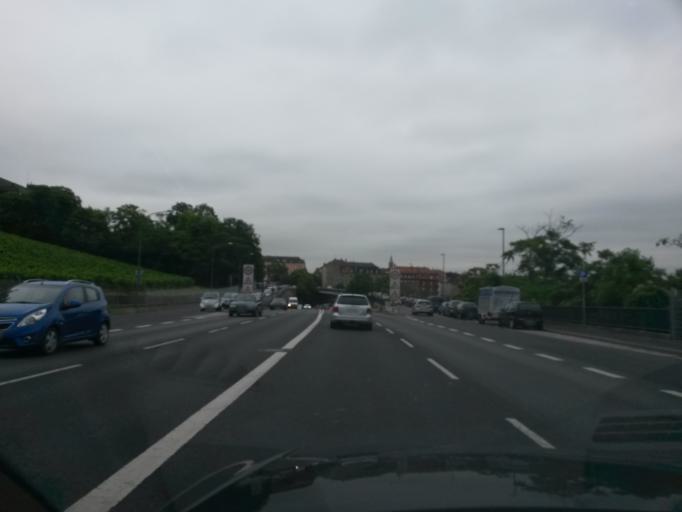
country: DE
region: Bavaria
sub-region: Regierungsbezirk Unterfranken
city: Wuerzburg
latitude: 49.8041
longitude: 9.9367
